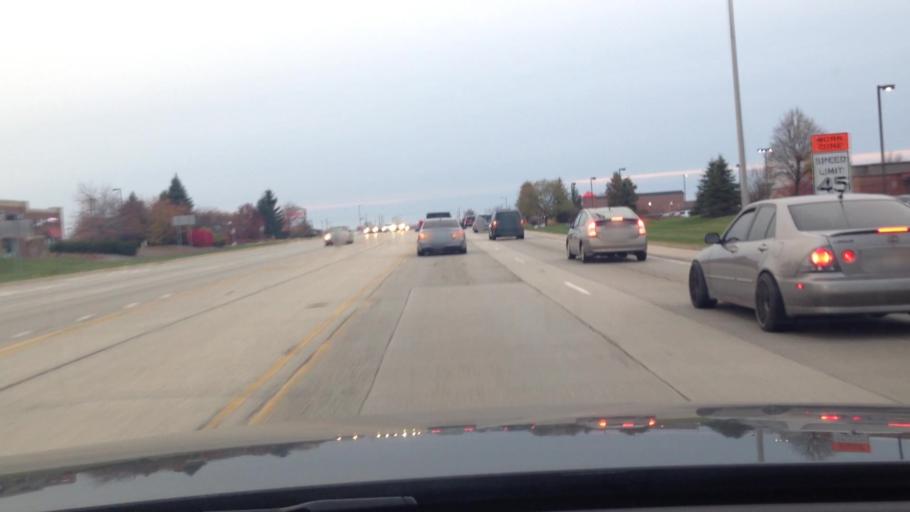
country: US
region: Illinois
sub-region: McHenry County
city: Lake in the Hills
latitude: 42.1696
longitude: -88.3353
